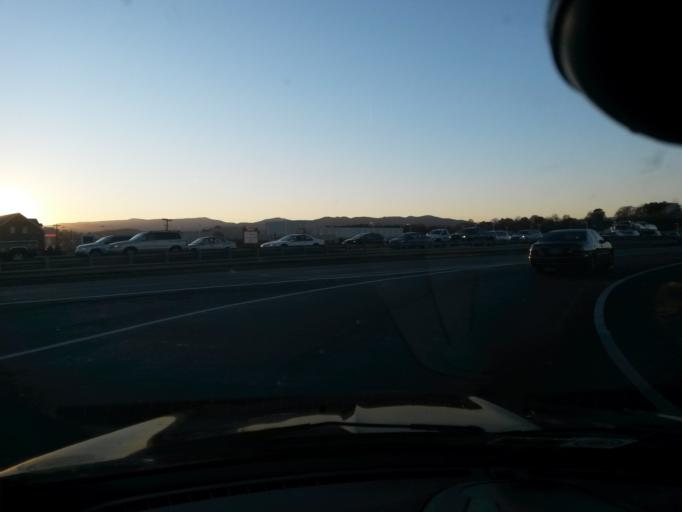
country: US
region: Virginia
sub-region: Roanoke County
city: Narrows
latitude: 37.2315
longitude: -79.9721
